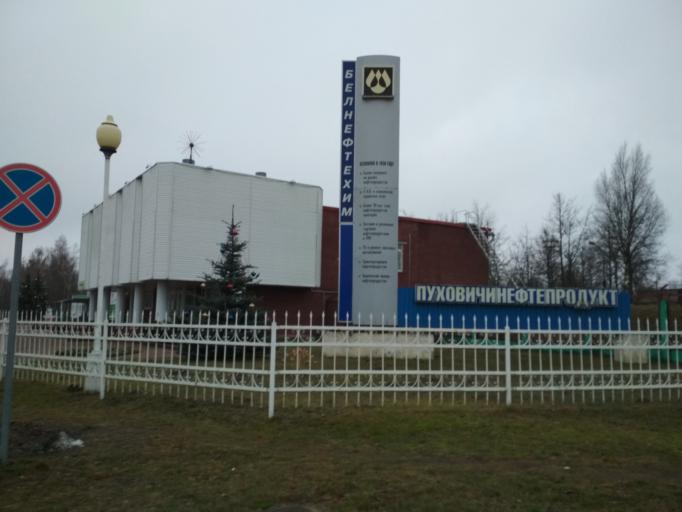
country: BY
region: Minsk
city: Mar''ina Horka
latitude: 53.4938
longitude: 28.1588
